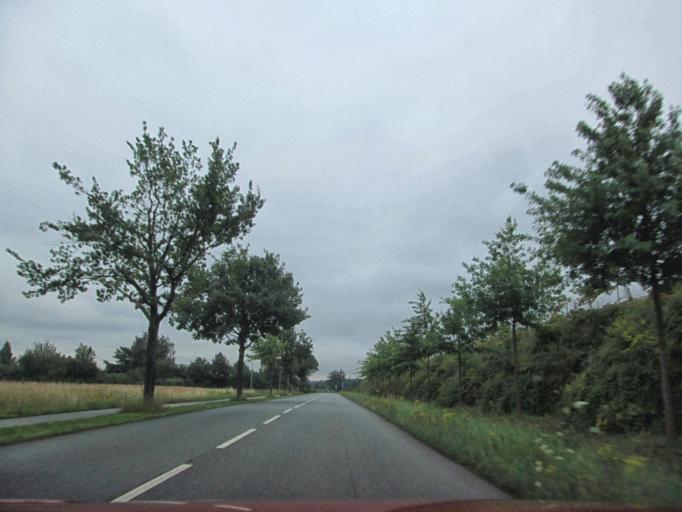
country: DE
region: Lower Saxony
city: Weyhausen
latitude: 52.4008
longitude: 10.7241
